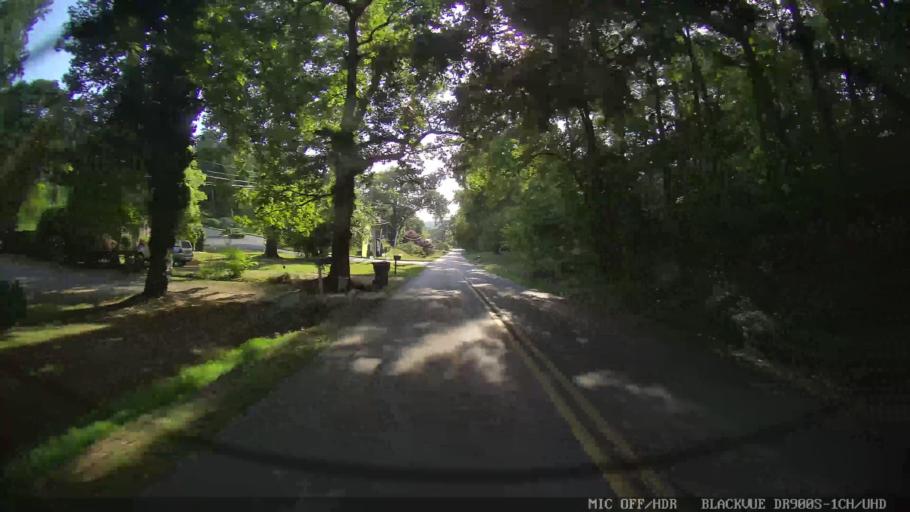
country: US
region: Georgia
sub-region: Floyd County
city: Rome
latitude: 34.2333
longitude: -85.1545
